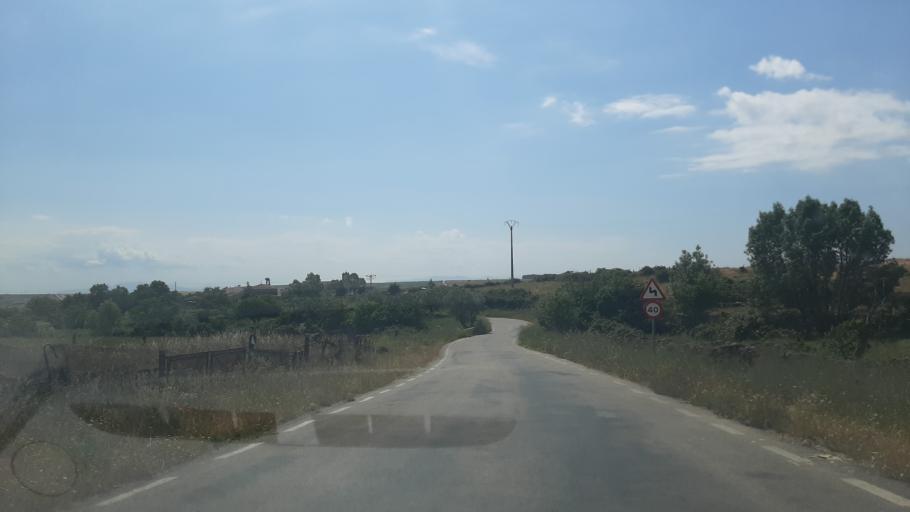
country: ES
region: Castille and Leon
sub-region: Provincia de Salamanca
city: Gallegos de Arganan
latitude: 40.6336
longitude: -6.7099
